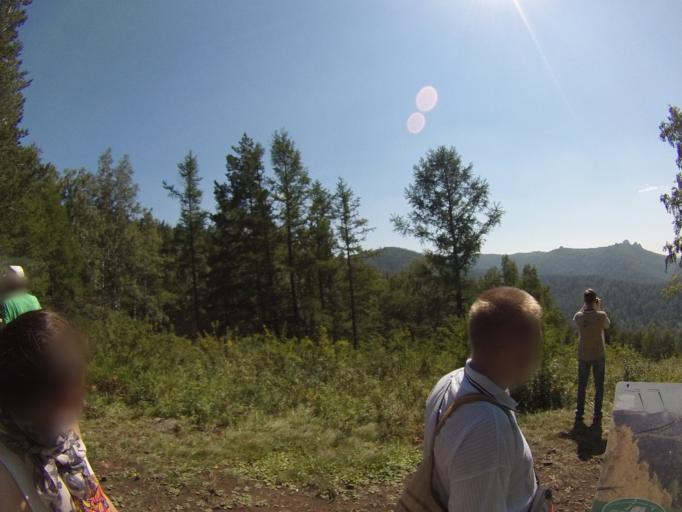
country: RU
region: Krasnoyarskiy
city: Krasnoyarsk
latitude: 55.9335
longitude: 92.7564
